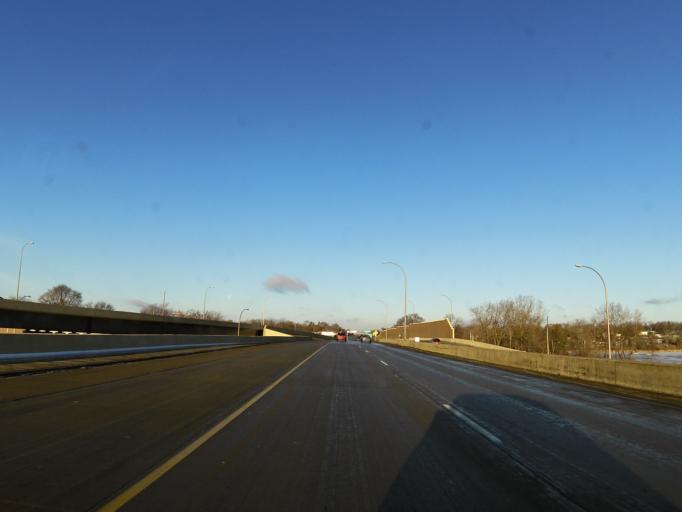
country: US
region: Minnesota
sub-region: Hennepin County
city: Richfield
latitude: 44.8905
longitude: -93.2943
